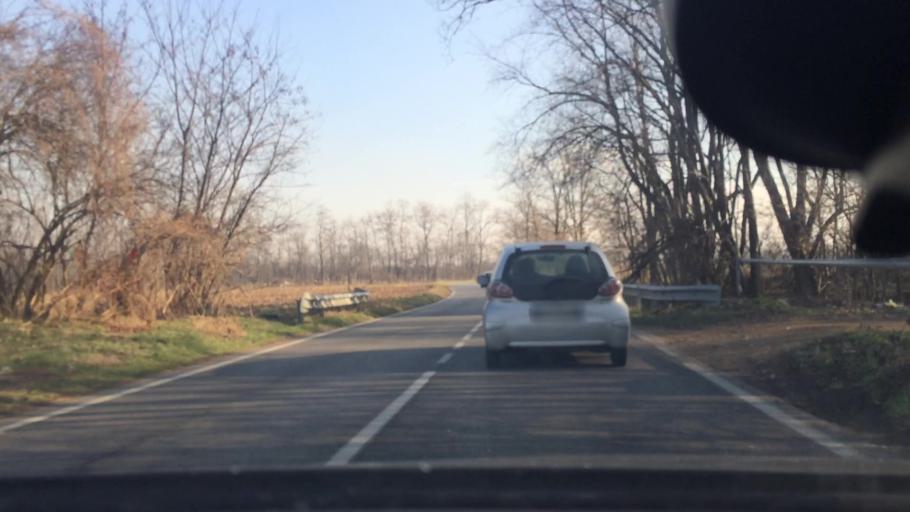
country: IT
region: Lombardy
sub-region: Citta metropolitana di Milano
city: Casorezzo
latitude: 45.5136
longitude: 8.9195
